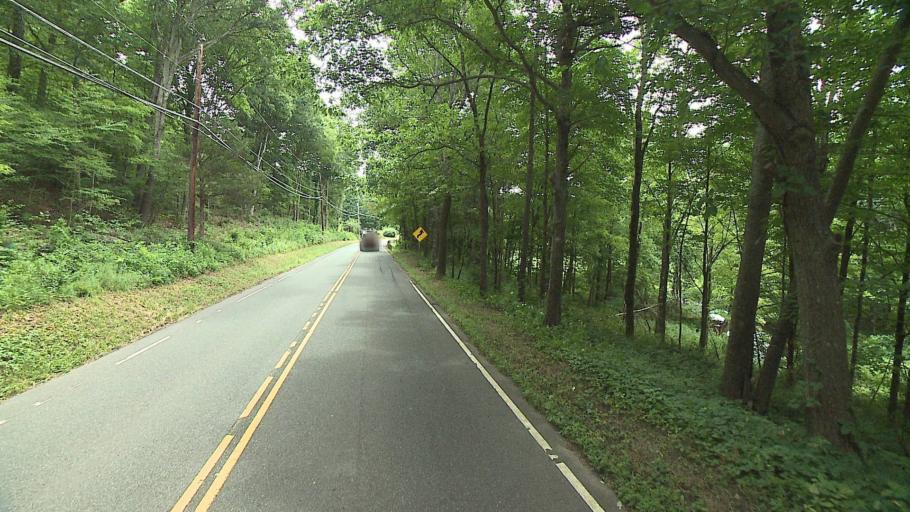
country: US
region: Connecticut
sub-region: Litchfield County
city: Woodbury
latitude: 41.5771
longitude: -73.2391
